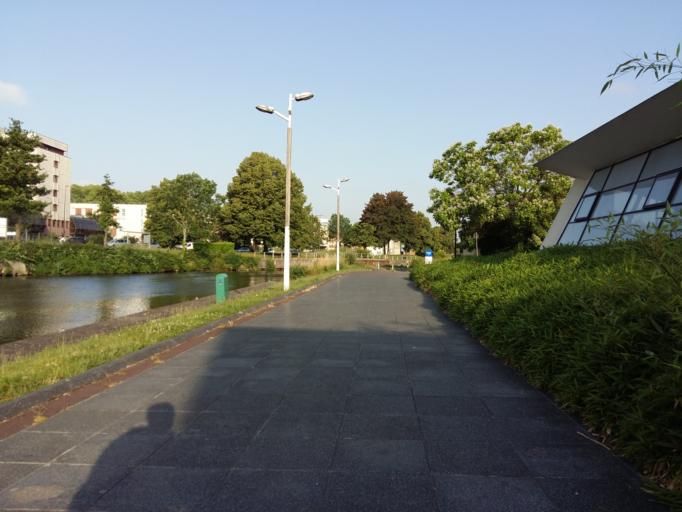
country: FR
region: Picardie
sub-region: Departement de la Somme
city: Amiens
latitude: 49.8995
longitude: 2.2908
